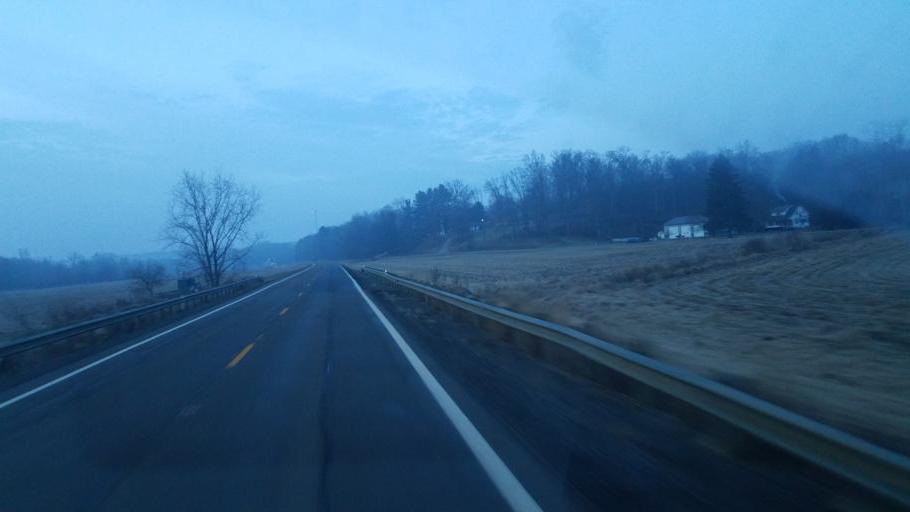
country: US
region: Ohio
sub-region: Coshocton County
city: West Lafayette
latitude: 40.3265
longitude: -81.7436
